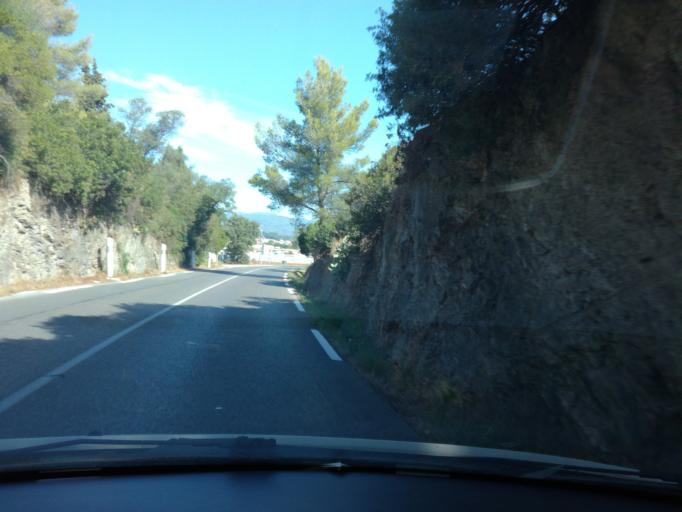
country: FR
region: Provence-Alpes-Cote d'Azur
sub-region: Departement du Var
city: La Crau
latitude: 43.1356
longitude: 6.0798
